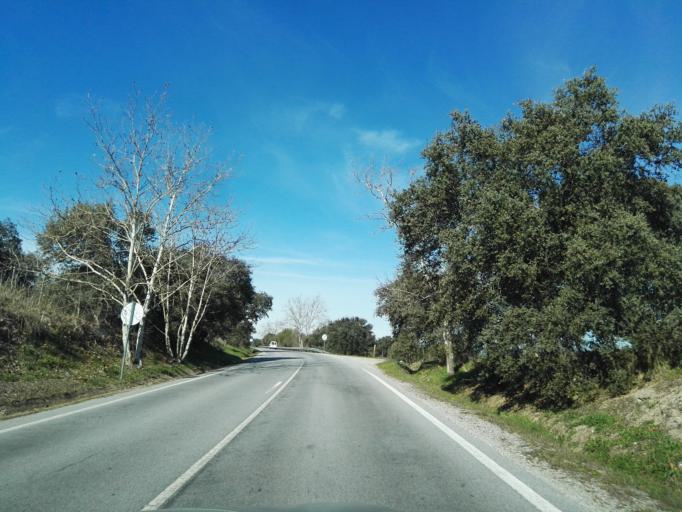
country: PT
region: Portalegre
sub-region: Arronches
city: Arronches
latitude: 39.0435
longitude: -7.2613
